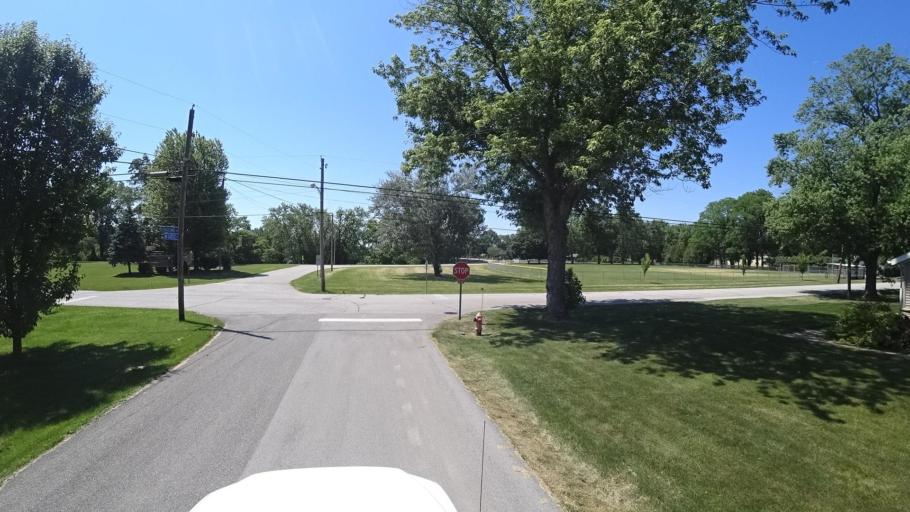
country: US
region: Indiana
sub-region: Porter County
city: Burns Harbor
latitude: 41.6106
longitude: -87.1138
